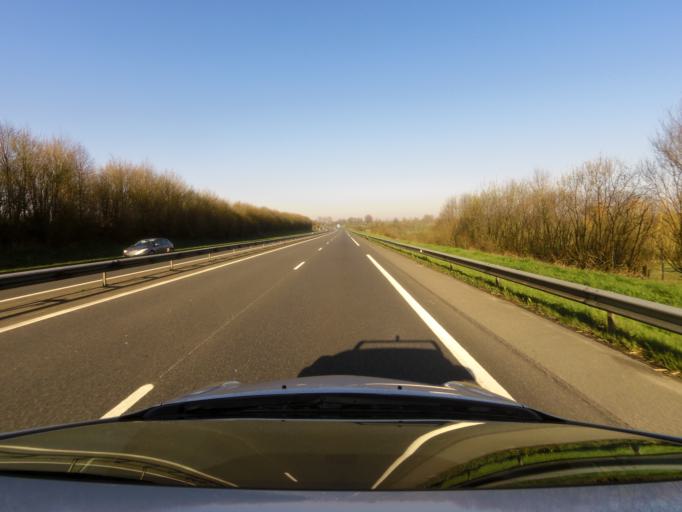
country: FR
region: Lower Normandy
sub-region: Departement du Calvados
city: Cahagnes
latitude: 49.0480
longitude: -0.7668
